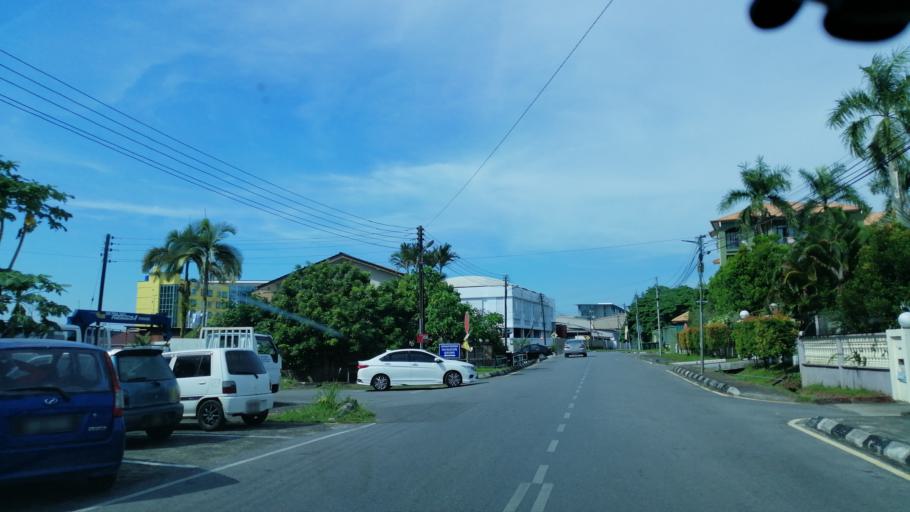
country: MY
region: Sarawak
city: Kuching
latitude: 1.5212
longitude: 110.3530
